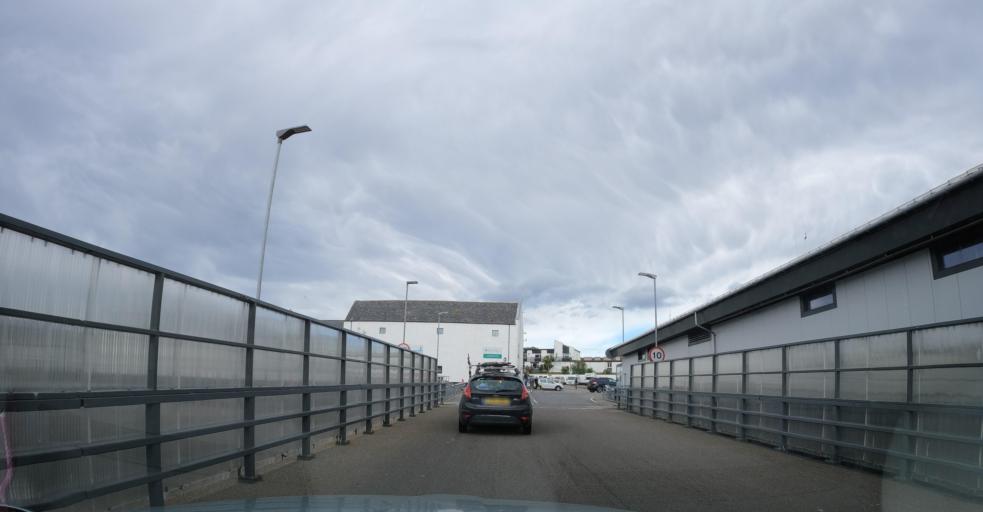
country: GB
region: Scotland
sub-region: Highland
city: Ullapool
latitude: 57.8947
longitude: -5.1604
